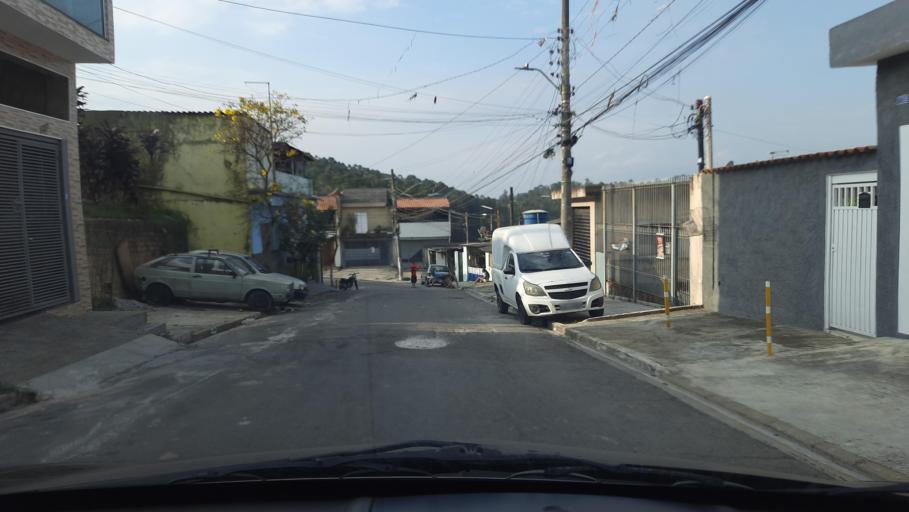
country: BR
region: Sao Paulo
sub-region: Caieiras
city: Caieiras
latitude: -23.4316
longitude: -46.7488
